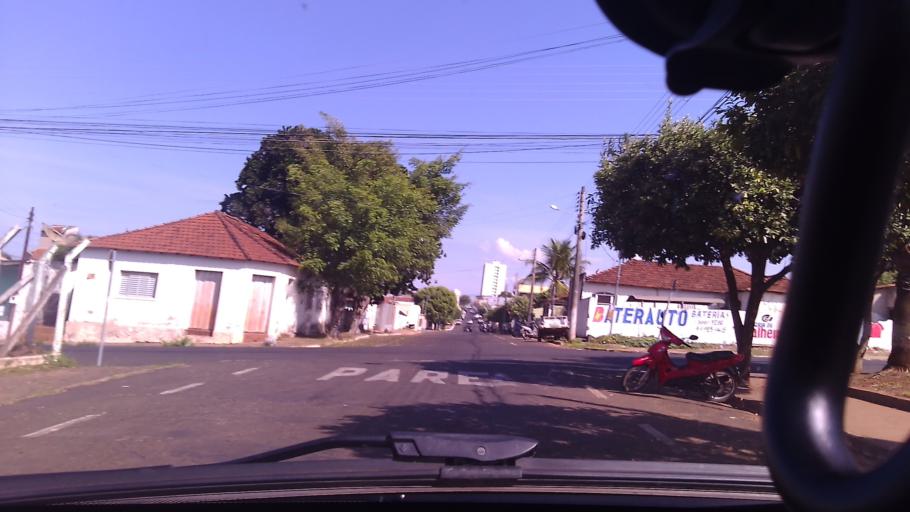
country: BR
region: Goias
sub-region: Mineiros
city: Mineiros
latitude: -17.5648
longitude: -52.5497
